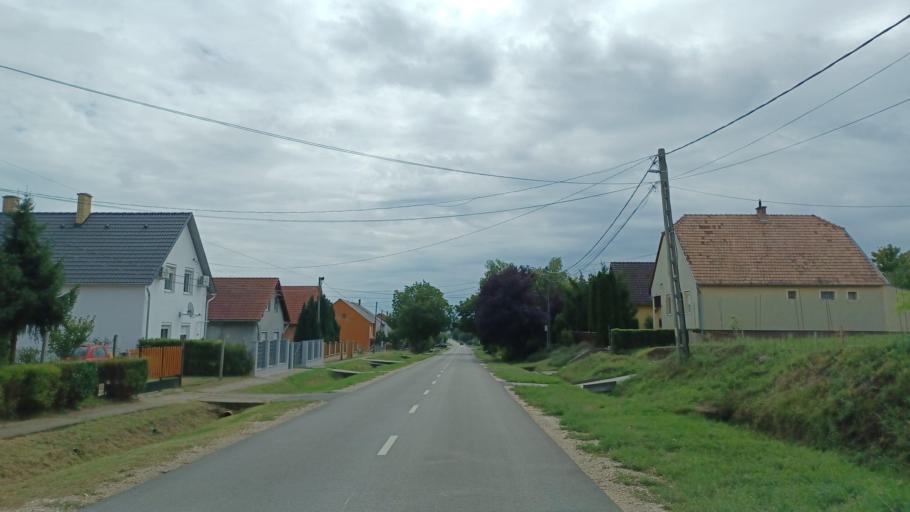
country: HU
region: Tolna
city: Szentgalpuszta
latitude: 46.4061
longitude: 18.6163
